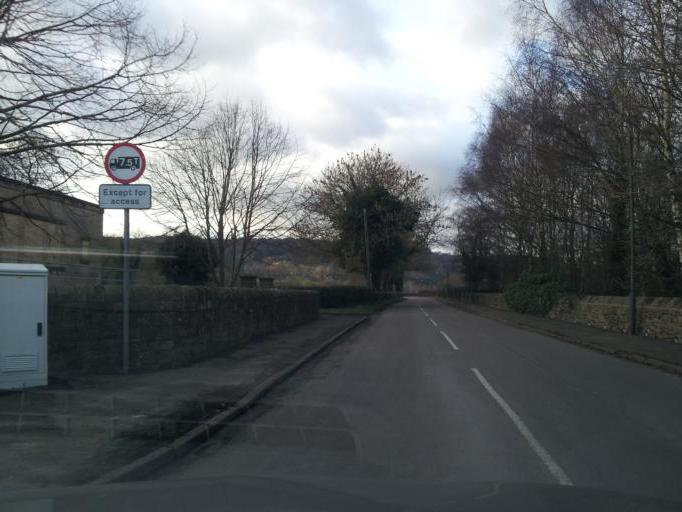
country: GB
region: England
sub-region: Derbyshire
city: Matlock
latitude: 53.1588
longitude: -1.5960
